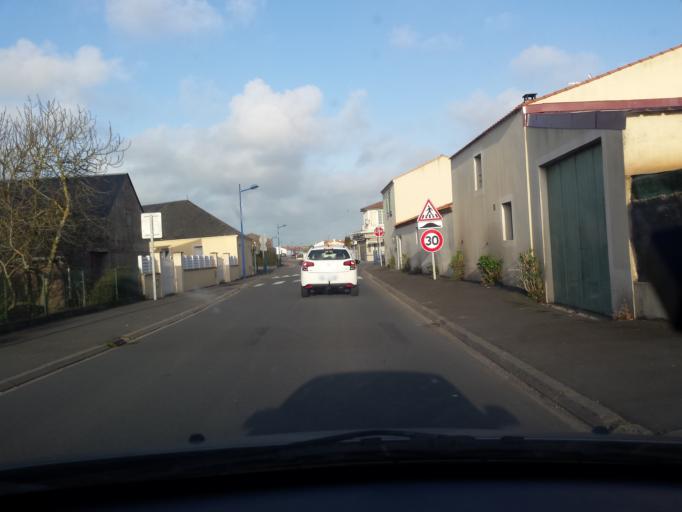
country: FR
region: Pays de la Loire
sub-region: Departement de la Vendee
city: Saint-Mathurin
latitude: 46.5641
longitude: -1.7157
